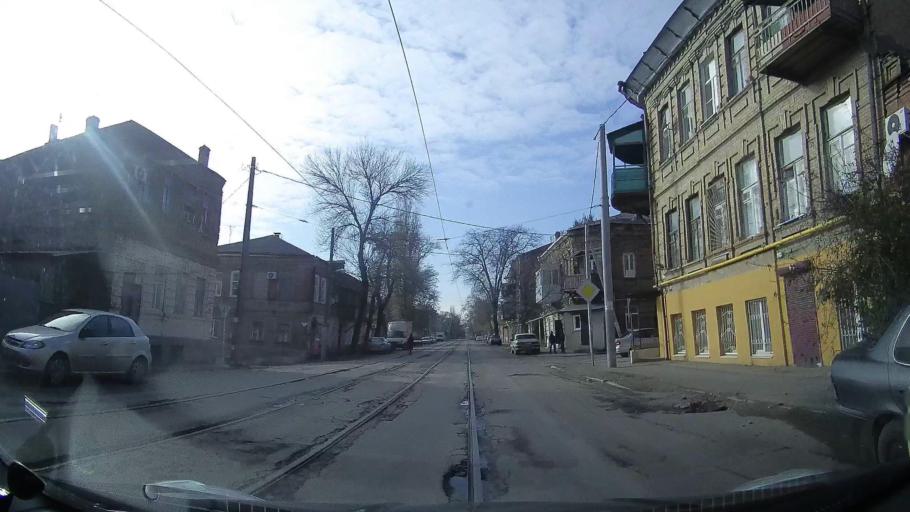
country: RU
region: Rostov
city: Rostov-na-Donu
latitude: 47.2208
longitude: 39.7277
